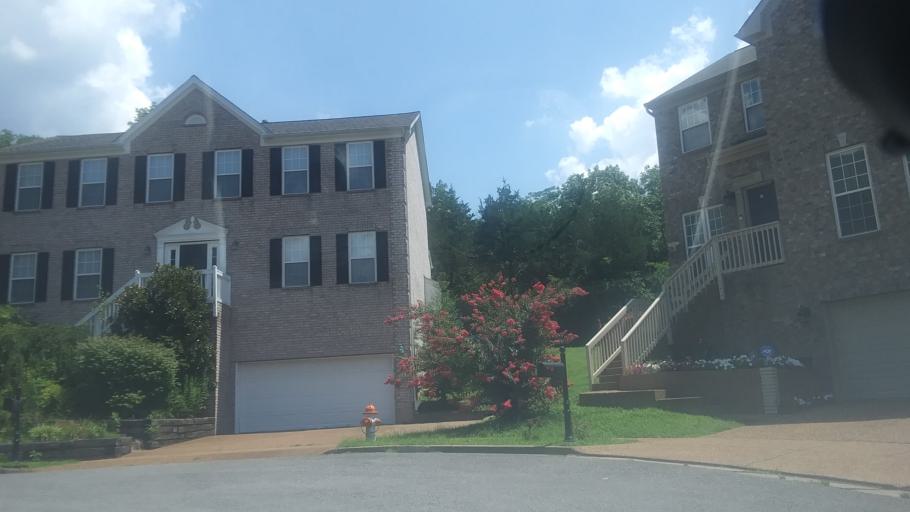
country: US
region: Tennessee
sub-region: Davidson County
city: Belle Meade
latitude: 36.1175
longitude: -86.9294
